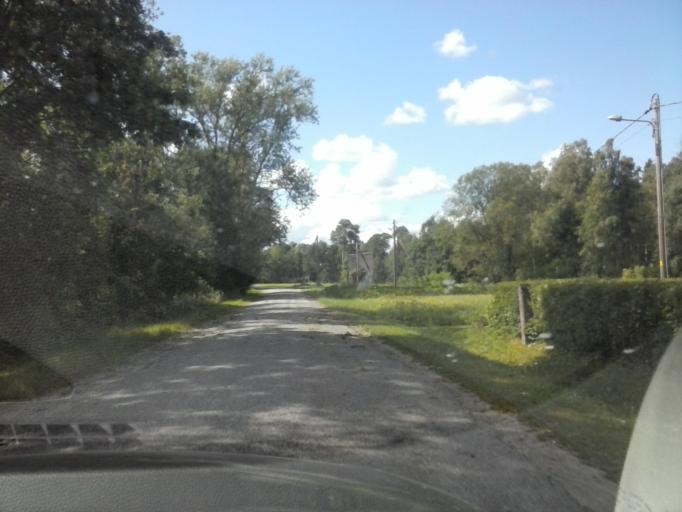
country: EE
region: Laeaene-Virumaa
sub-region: Vaeike-Maarja vald
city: Vaike-Maarja
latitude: 59.0855
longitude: 26.1827
